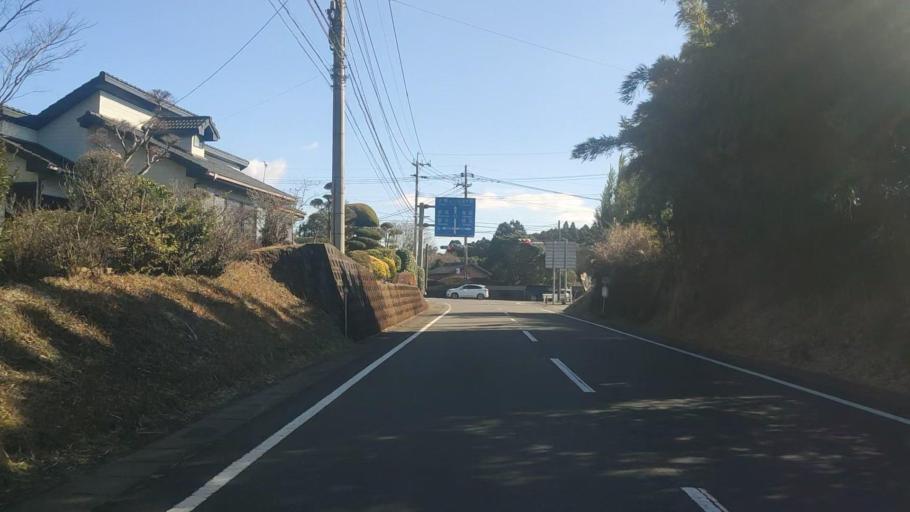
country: JP
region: Kagoshima
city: Kokubu-matsuki
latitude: 31.6696
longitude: 130.8444
